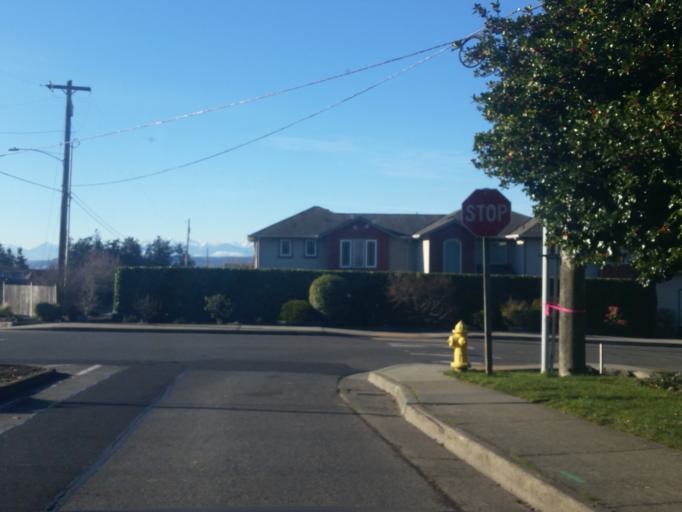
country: US
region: Washington
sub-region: Snohomish County
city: Edmonds
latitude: 47.8216
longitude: -122.3668
